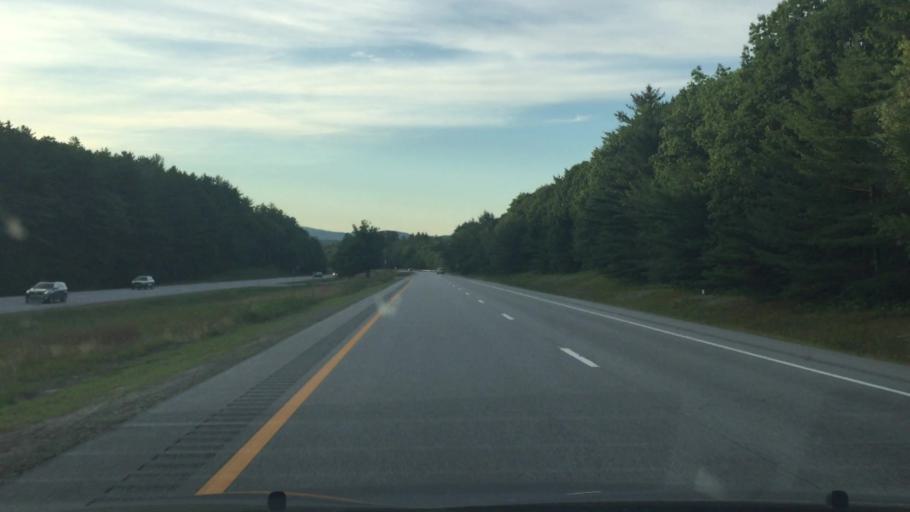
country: US
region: New Hampshire
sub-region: Grafton County
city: Plymouth
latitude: 43.7358
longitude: -71.6588
